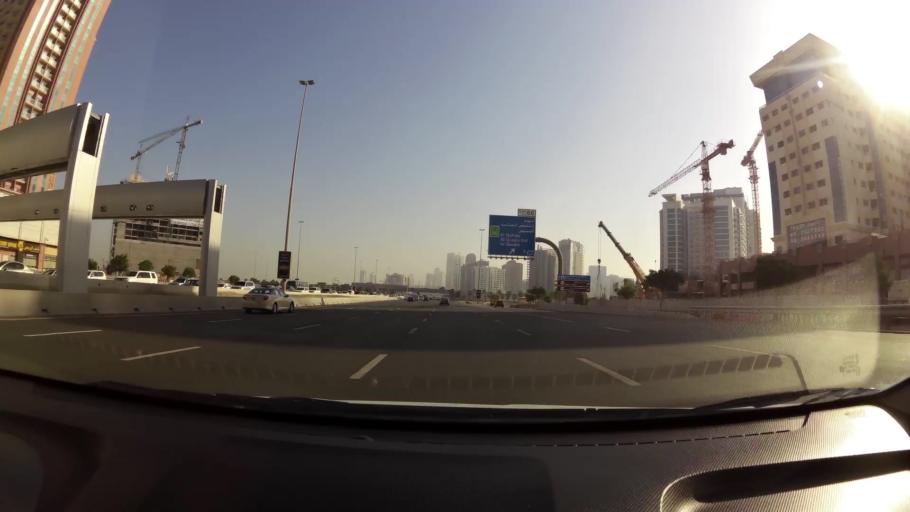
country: AE
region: Ash Shariqah
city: Sharjah
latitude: 25.2859
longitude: 55.3594
